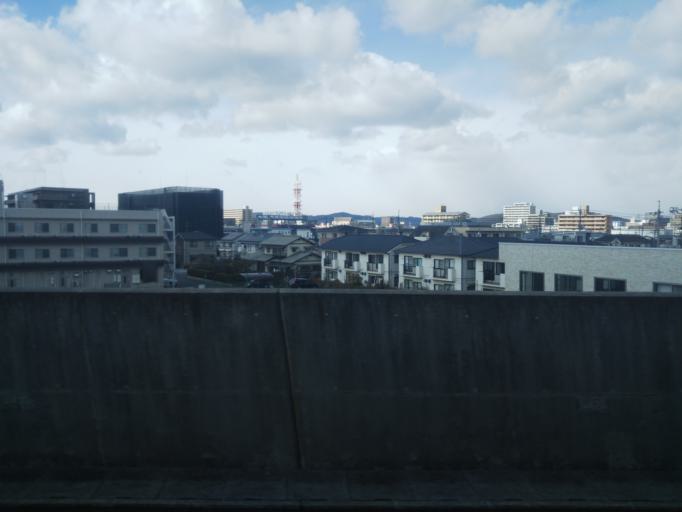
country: JP
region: Okayama
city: Okayama-shi
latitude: 34.6356
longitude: 133.9039
